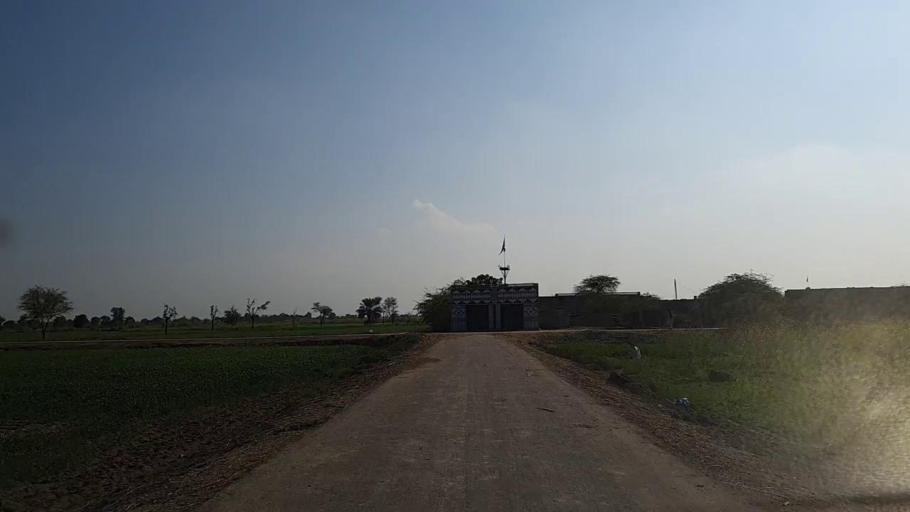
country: PK
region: Sindh
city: Jam Sahib
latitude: 26.2794
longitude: 68.6136
